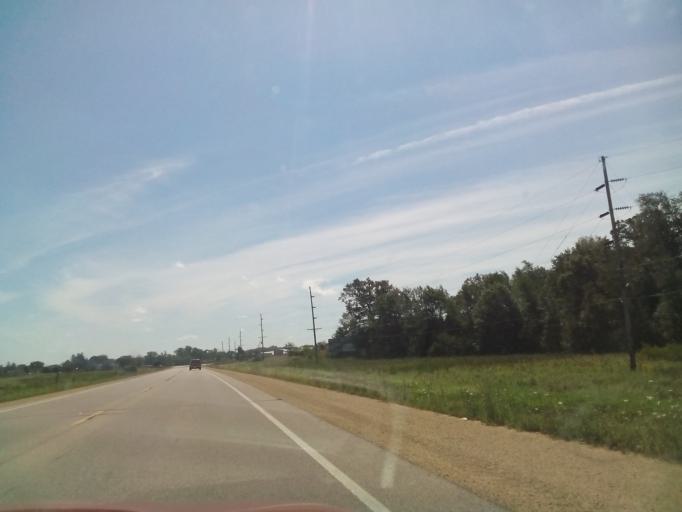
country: US
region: Wisconsin
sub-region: Green County
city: Monticello
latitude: 42.7526
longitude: -89.6058
